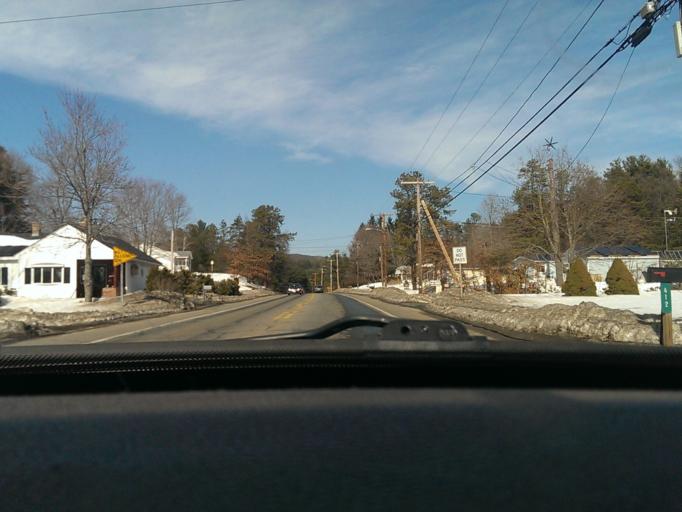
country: US
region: Massachusetts
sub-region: Hampshire County
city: Ware
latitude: 42.2333
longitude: -72.2909
